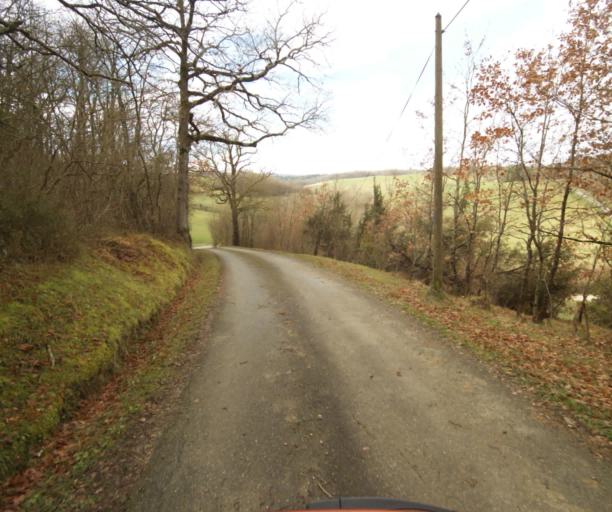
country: FR
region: Midi-Pyrenees
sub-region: Departement de l'Ariege
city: Pamiers
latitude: 43.1000
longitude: 1.5398
